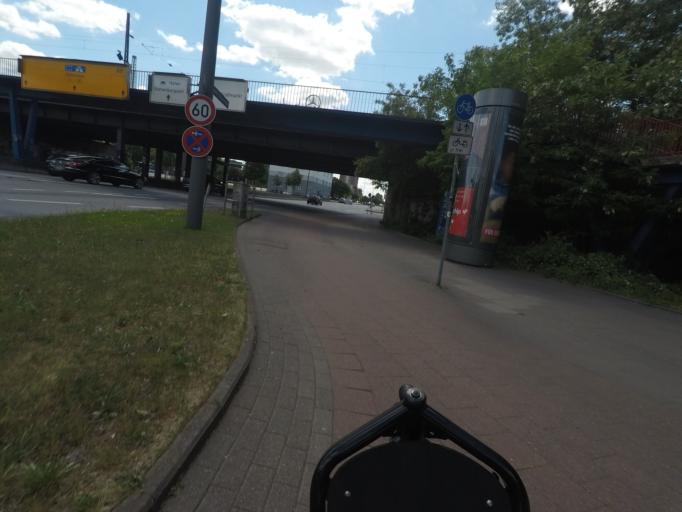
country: DE
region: Hamburg
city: Hammerbrook
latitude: 53.5401
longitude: 10.0317
